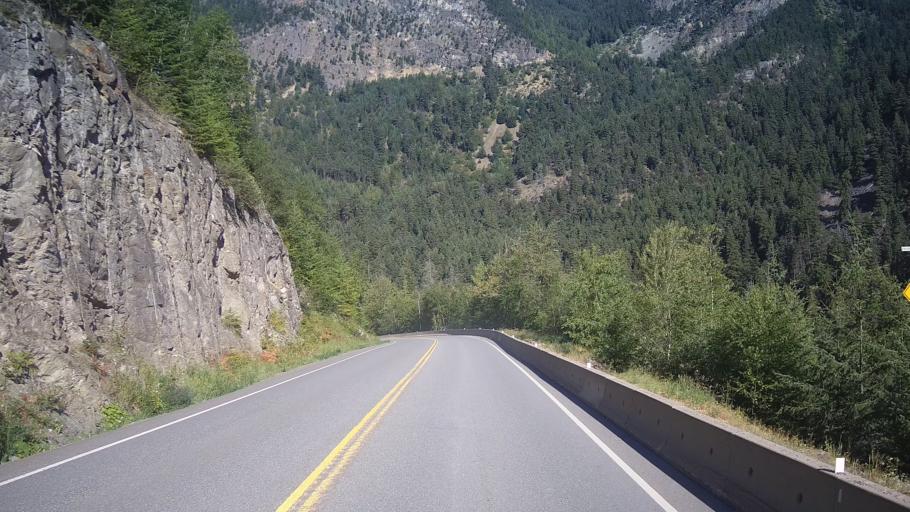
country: CA
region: British Columbia
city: Lillooet
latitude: 50.6384
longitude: -122.0823
